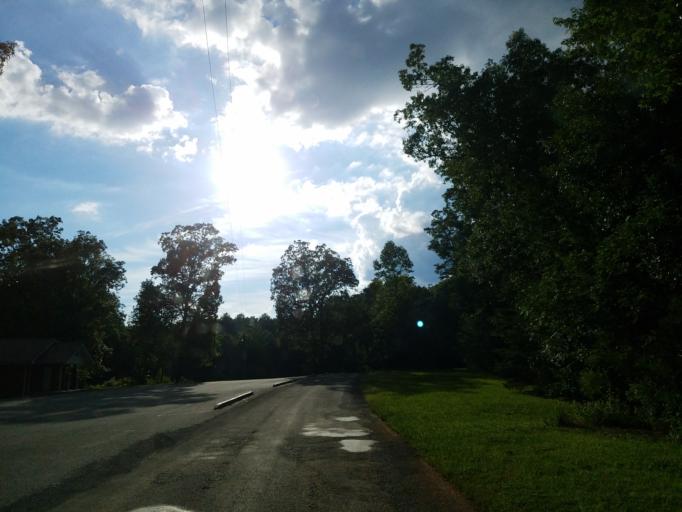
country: US
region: Georgia
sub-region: Gilmer County
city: Ellijay
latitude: 34.6532
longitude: -84.2918
